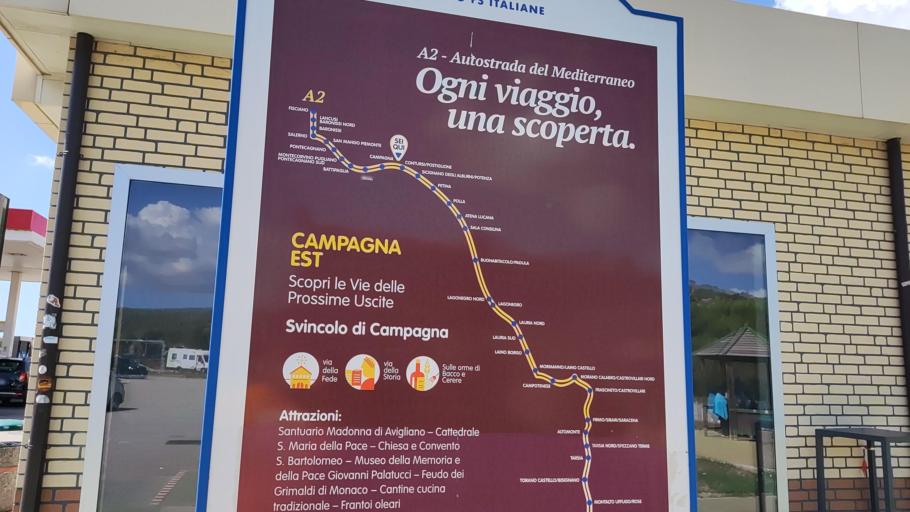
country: IT
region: Campania
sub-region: Provincia di Salerno
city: Serre
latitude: 40.6183
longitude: 15.1656
